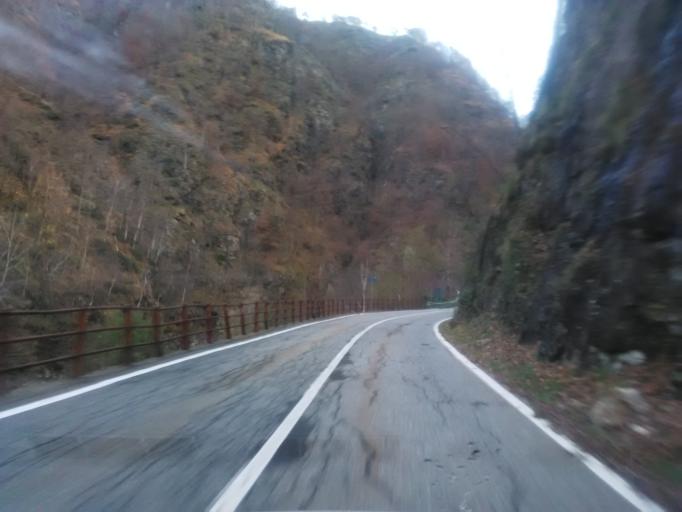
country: IT
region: Piedmont
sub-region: Provincia di Vercelli
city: Cravagliana
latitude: 45.8695
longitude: 8.1858
